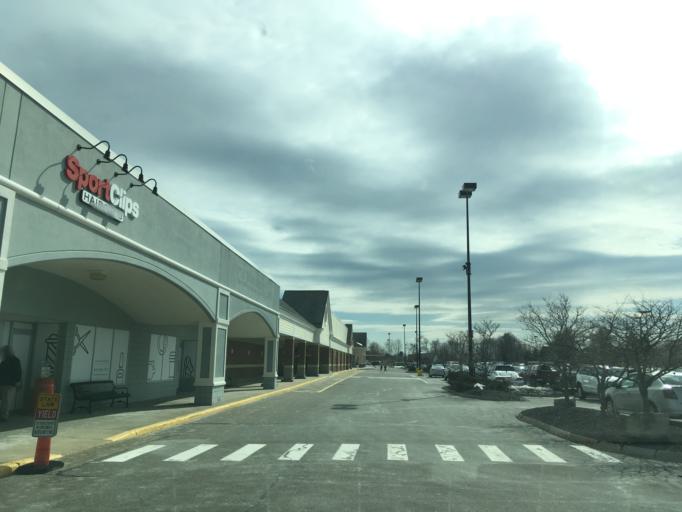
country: US
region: New Hampshire
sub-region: Rockingham County
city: North Hampton
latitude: 42.9685
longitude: -70.8341
